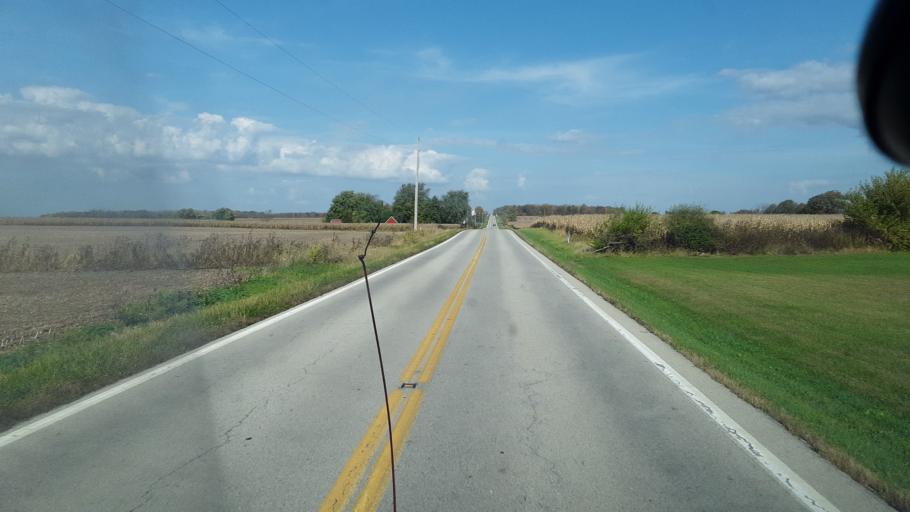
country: US
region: Ohio
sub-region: Clinton County
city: Sabina
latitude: 39.5216
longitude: -83.6960
